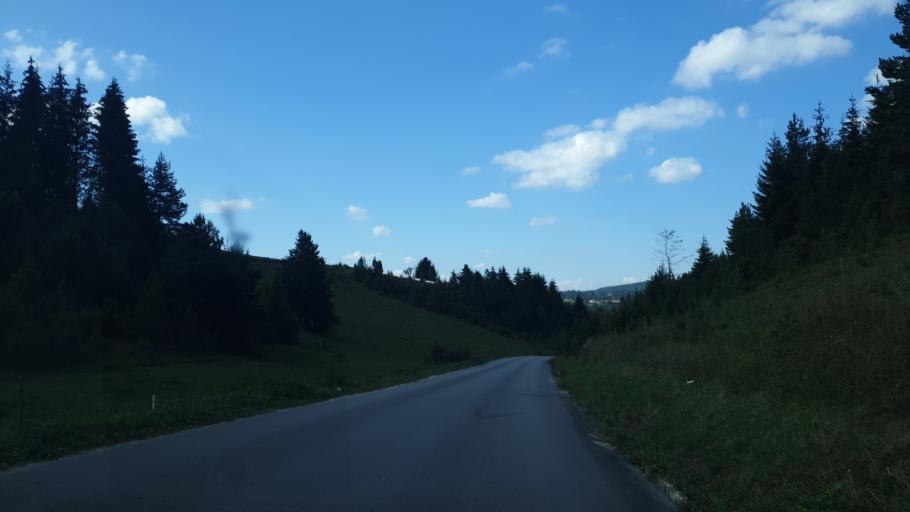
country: RS
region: Central Serbia
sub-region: Zlatiborski Okrug
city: Nova Varos
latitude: 43.4289
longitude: 19.8734
